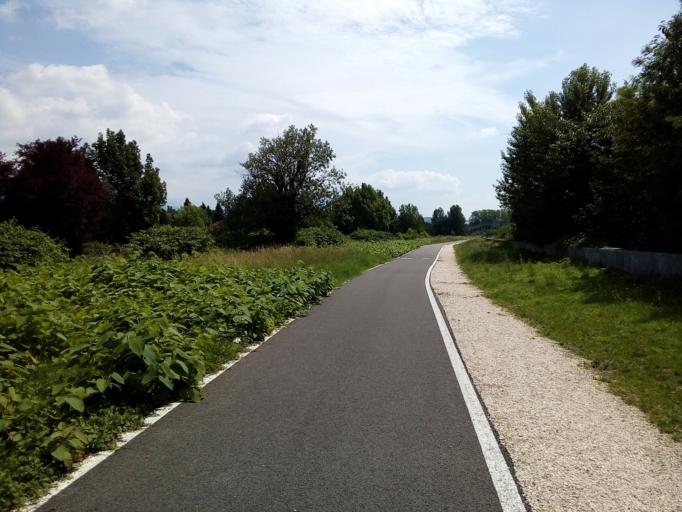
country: FR
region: Rhone-Alpes
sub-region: Departement de l'Isere
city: La Tronche
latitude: 45.1959
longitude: 5.7437
